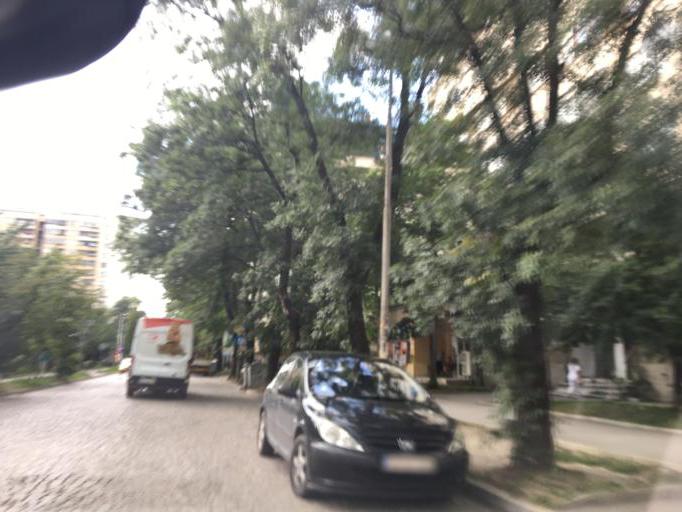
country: BG
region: Sofia-Capital
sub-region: Stolichna Obshtina
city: Sofia
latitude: 42.6842
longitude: 23.2981
